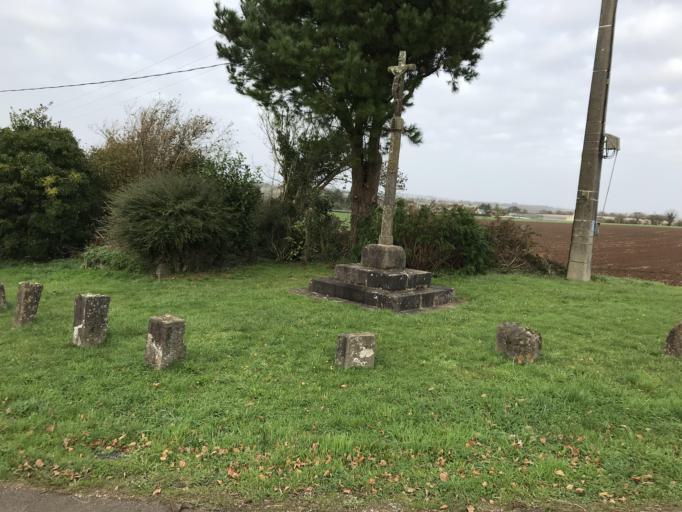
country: FR
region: Brittany
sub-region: Departement du Finistere
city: Irvillac
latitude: 48.3581
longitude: -4.2102
